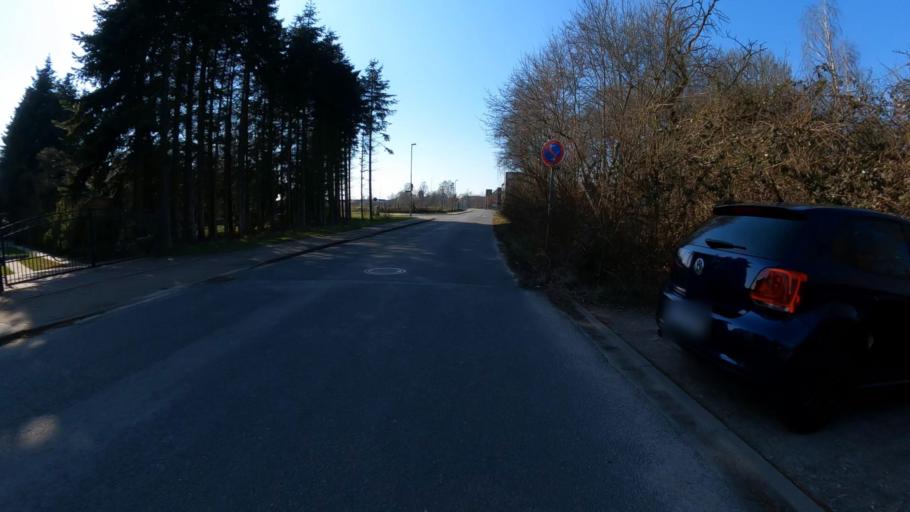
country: DE
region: Lower Saxony
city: Buchholz in der Nordheide
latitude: 53.3239
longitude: 9.8793
